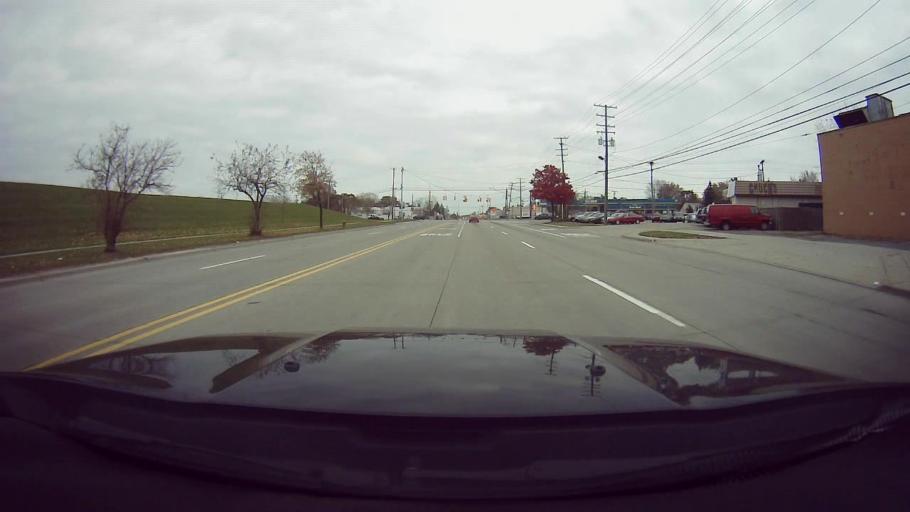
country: US
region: Michigan
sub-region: Macomb County
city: Warren
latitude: 42.4638
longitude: -82.9930
